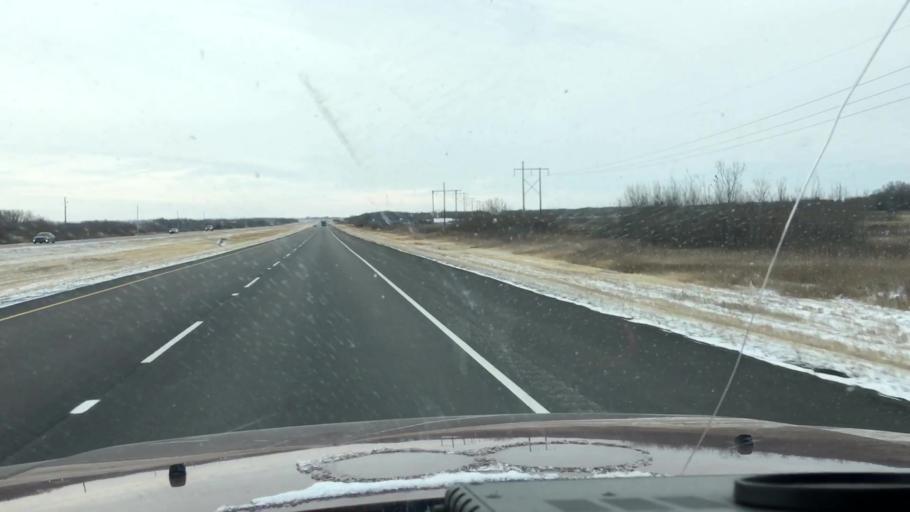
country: CA
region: Saskatchewan
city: Saskatoon
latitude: 51.8901
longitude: -106.5168
